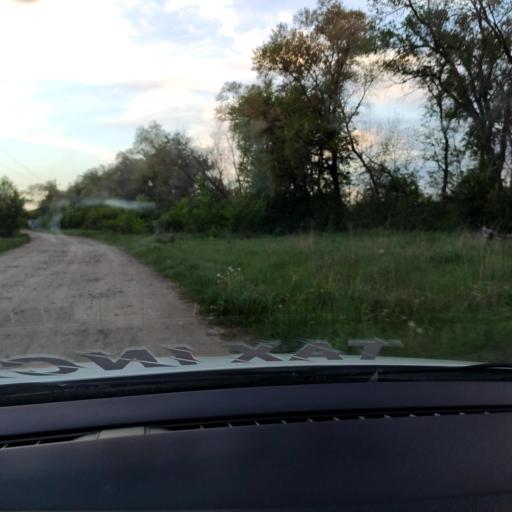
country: RU
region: Voronezj
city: Kolodeznyy
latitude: 51.4353
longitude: 39.2322
